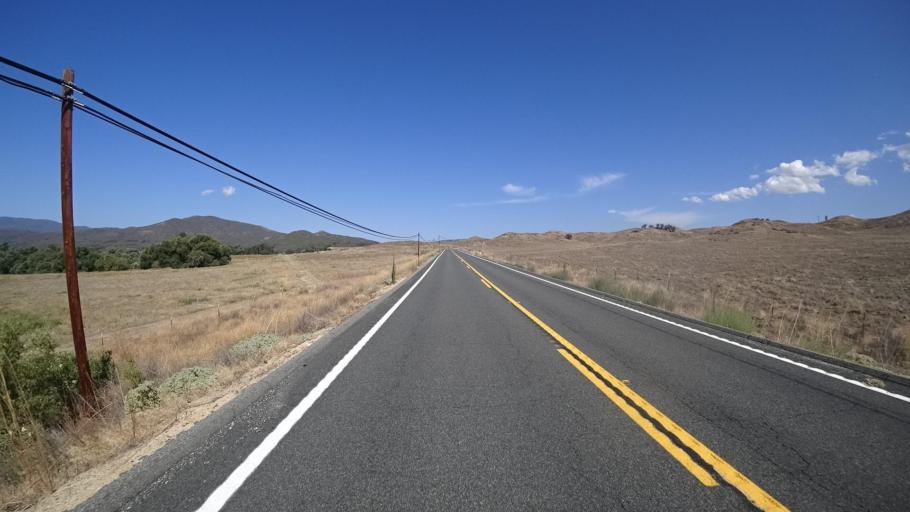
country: US
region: California
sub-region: Riverside County
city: Aguanga
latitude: 33.2993
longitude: -116.6899
